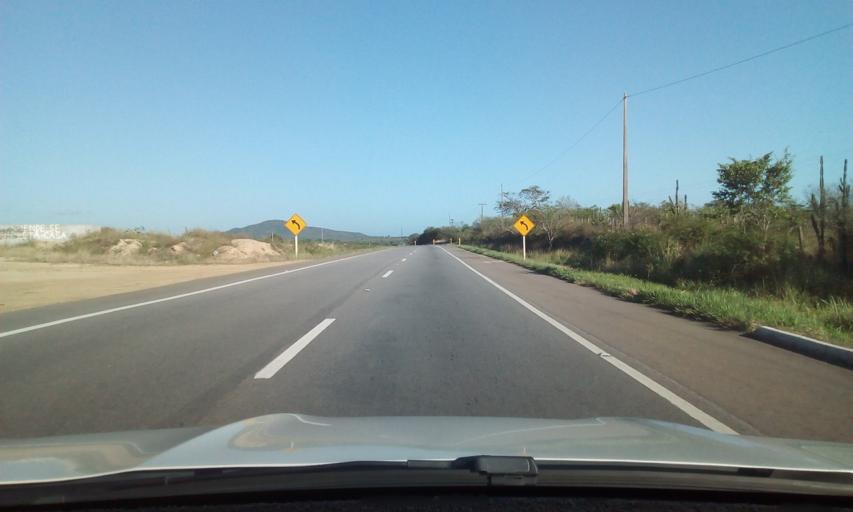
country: BR
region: Paraiba
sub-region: Gurinhem
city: Gurinhem
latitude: -7.1662
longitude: -35.3380
